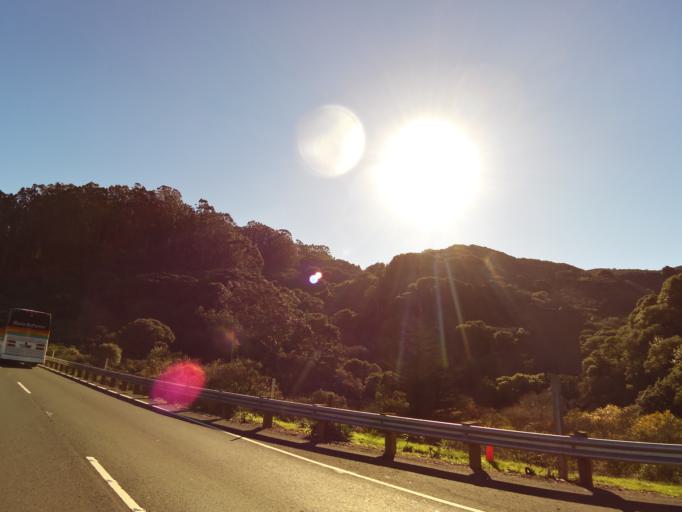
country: US
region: California
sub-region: Marin County
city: Sausalito
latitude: 37.8575
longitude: -122.4989
